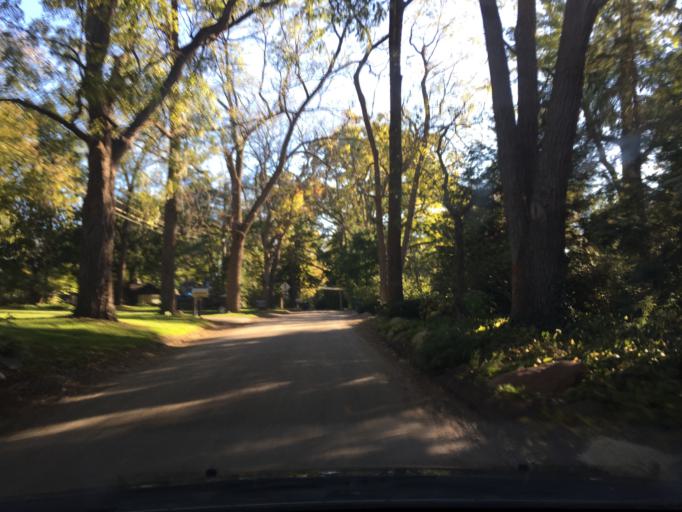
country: US
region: Michigan
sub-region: Oakland County
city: Franklin
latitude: 42.5535
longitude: -83.2933
